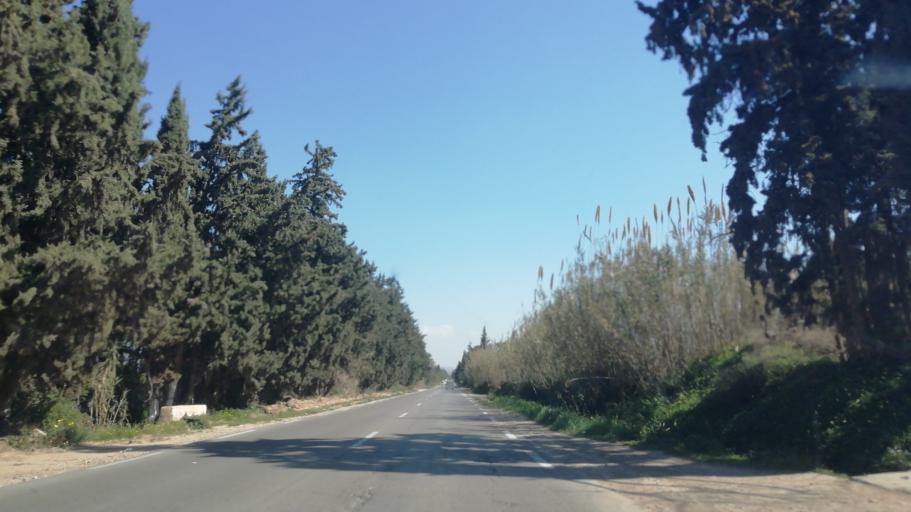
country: DZ
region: Mascara
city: Sig
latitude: 35.5796
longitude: 0.0152
